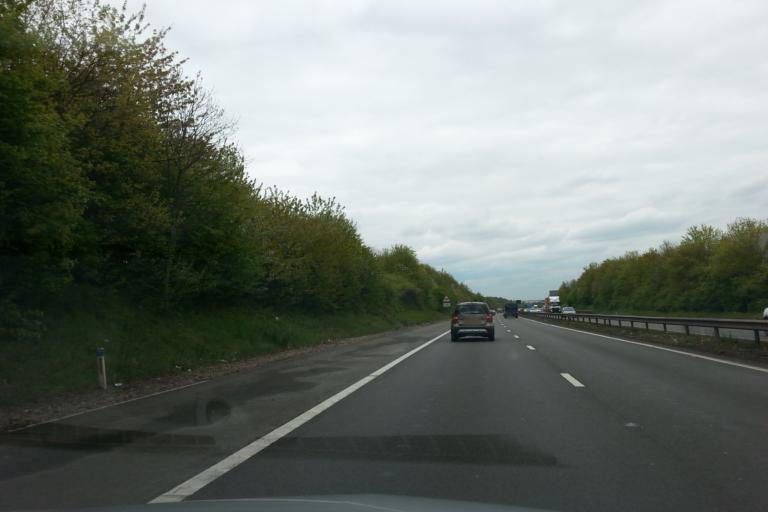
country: GB
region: England
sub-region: Staffordshire
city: Tamworth
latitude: 52.6194
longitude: -1.6303
